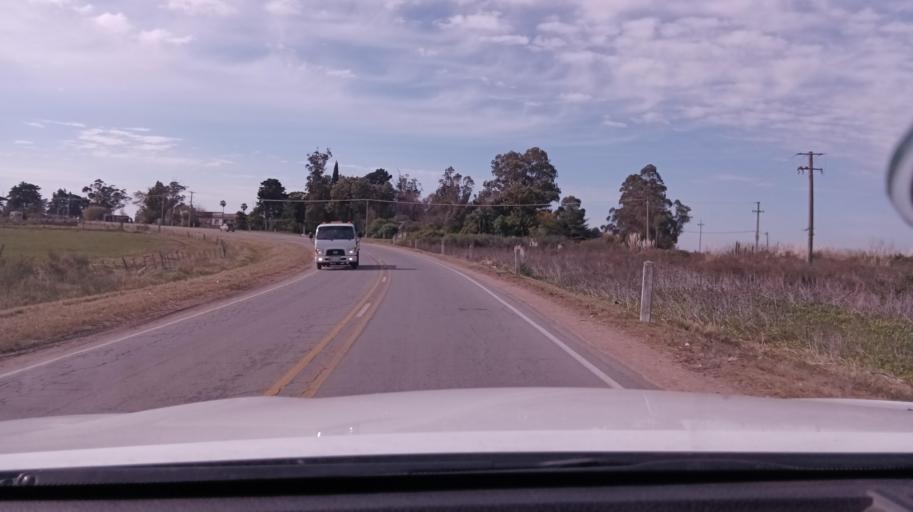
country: UY
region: Canelones
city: Toledo
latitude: -34.7073
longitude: -56.1060
